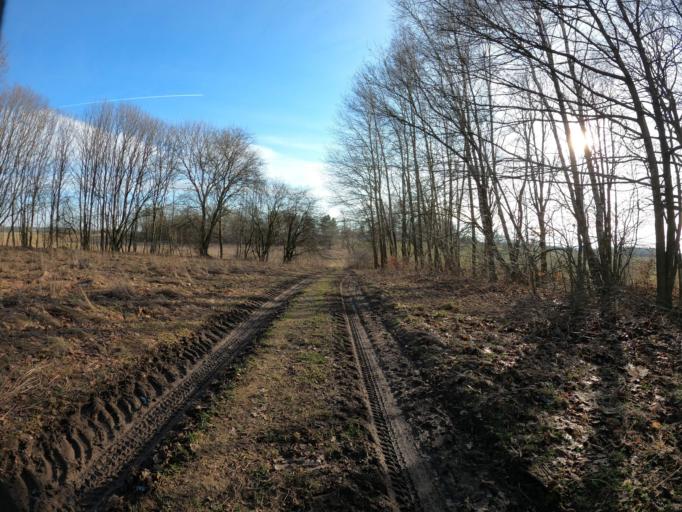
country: PL
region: West Pomeranian Voivodeship
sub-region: Powiat koszalinski
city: Polanow
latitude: 54.2044
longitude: 16.6520
